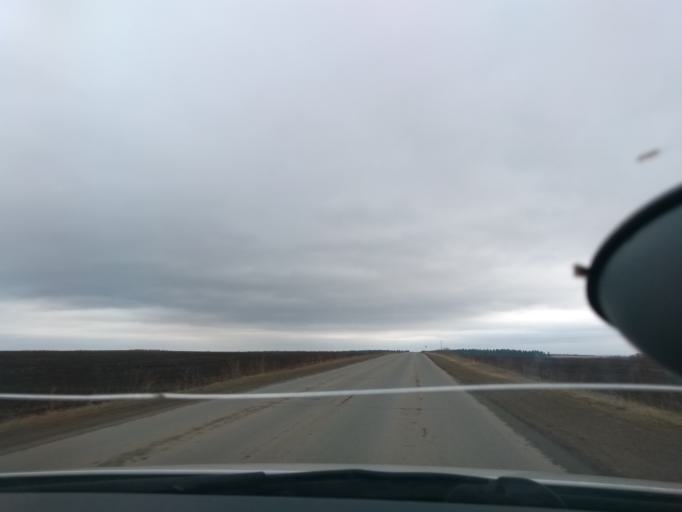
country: RU
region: Perm
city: Kungur
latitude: 57.3832
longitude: 56.8546
